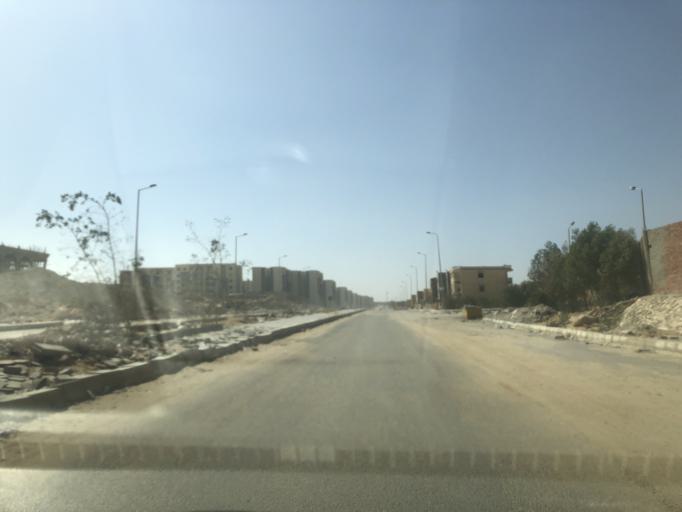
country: EG
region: Al Jizah
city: Madinat Sittah Uktubar
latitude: 29.9278
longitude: 30.9936
